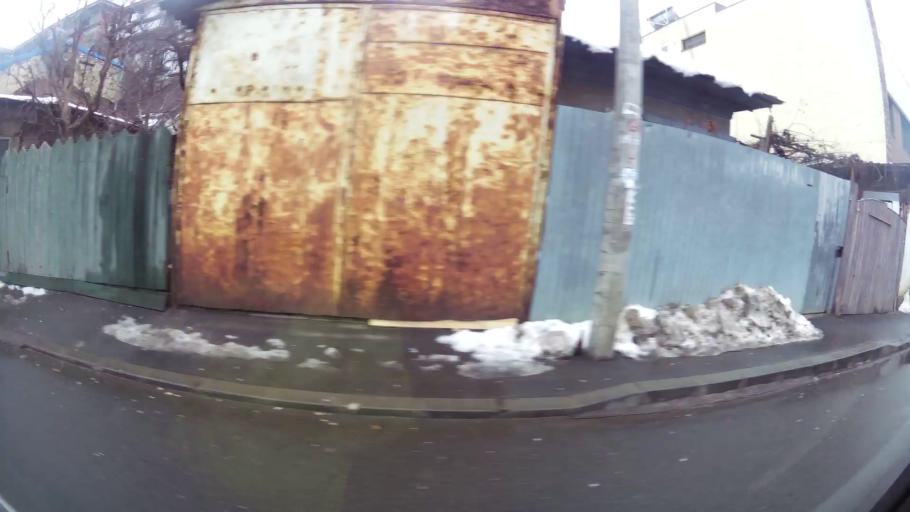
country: RO
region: Bucuresti
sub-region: Municipiul Bucuresti
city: Bucharest
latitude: 44.4127
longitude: 26.1268
